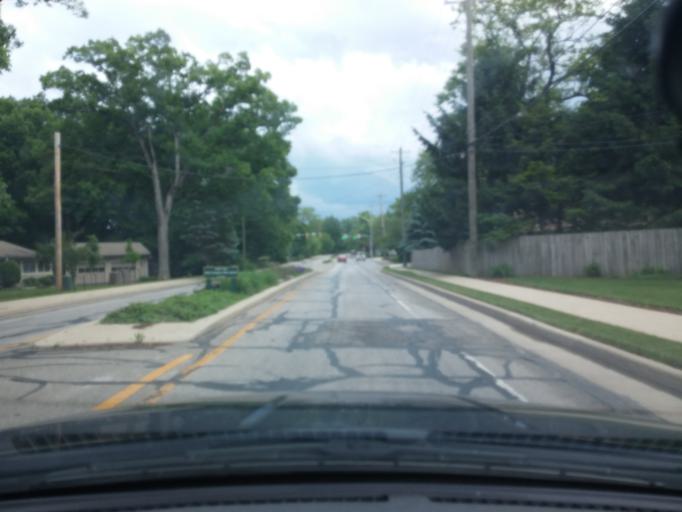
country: US
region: Indiana
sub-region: Tippecanoe County
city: West Lafayette
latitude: 40.4426
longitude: -86.9120
